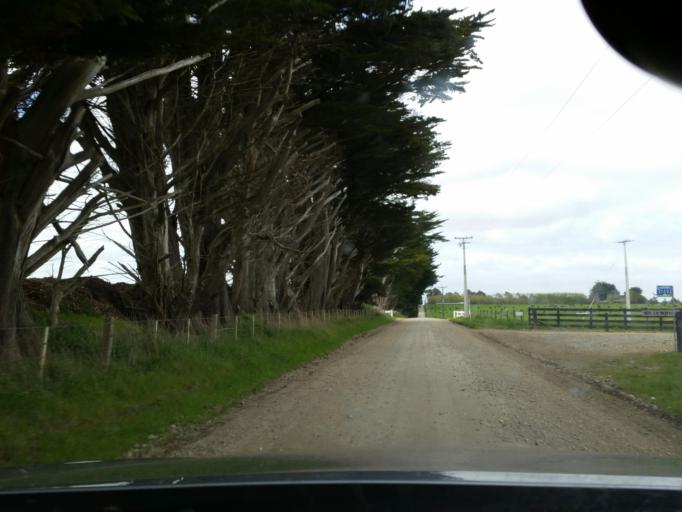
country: NZ
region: Southland
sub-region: Invercargill City
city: Invercargill
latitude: -46.3132
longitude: 168.4788
